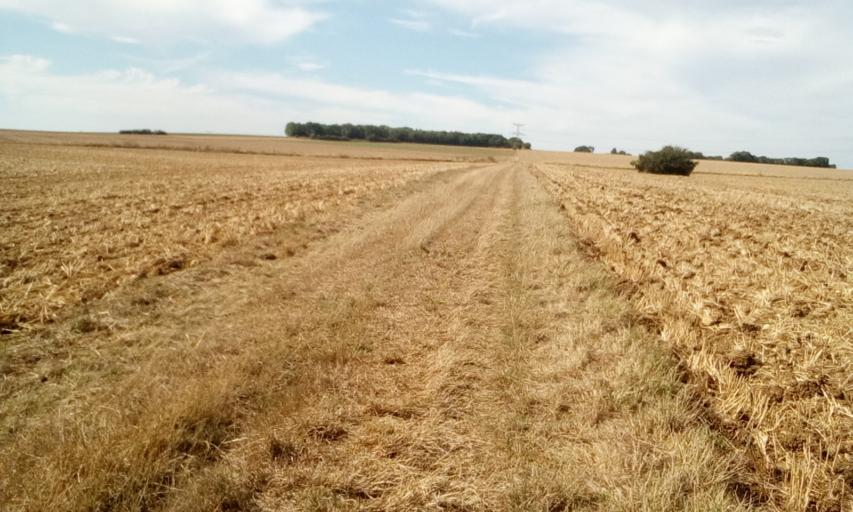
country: FR
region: Lower Normandy
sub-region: Departement du Calvados
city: Fontaine-Etoupefour
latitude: 49.1132
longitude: -0.4503
